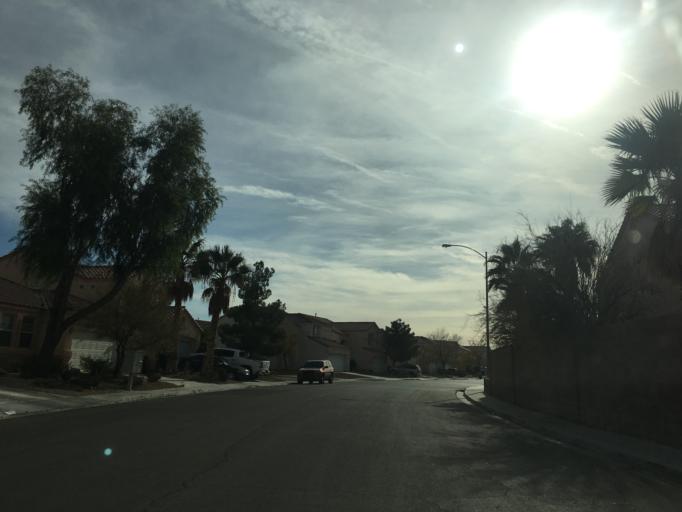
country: US
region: Nevada
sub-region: Clark County
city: Enterprise
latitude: 36.0165
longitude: -115.1661
